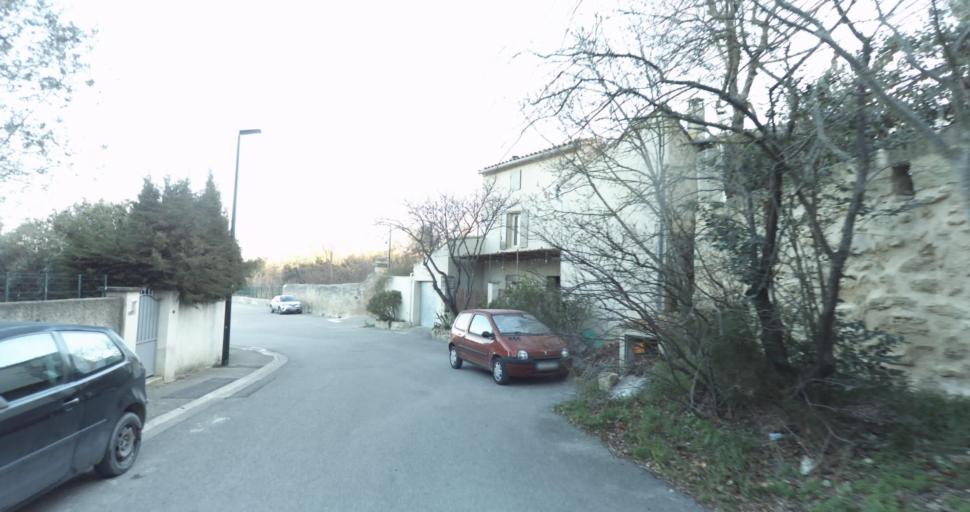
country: FR
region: Provence-Alpes-Cote d'Azur
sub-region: Departement des Bouches-du-Rhone
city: Barbentane
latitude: 43.9001
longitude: 4.7456
